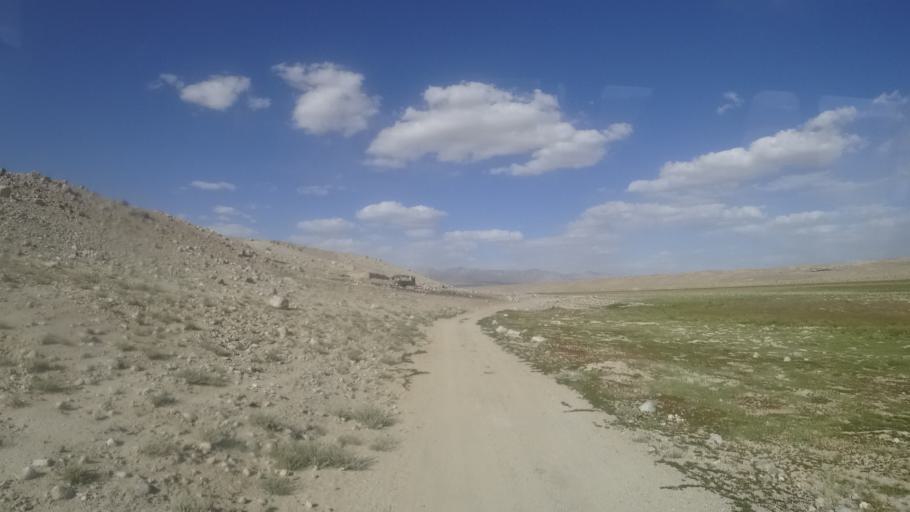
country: AF
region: Badakhshan
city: Khandud
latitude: 37.4164
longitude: 73.2290
